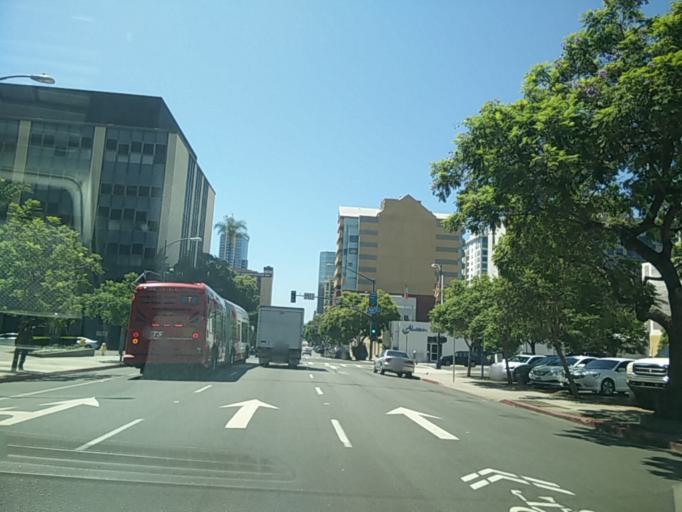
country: US
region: California
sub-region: San Diego County
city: San Diego
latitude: 32.7200
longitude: -117.1641
